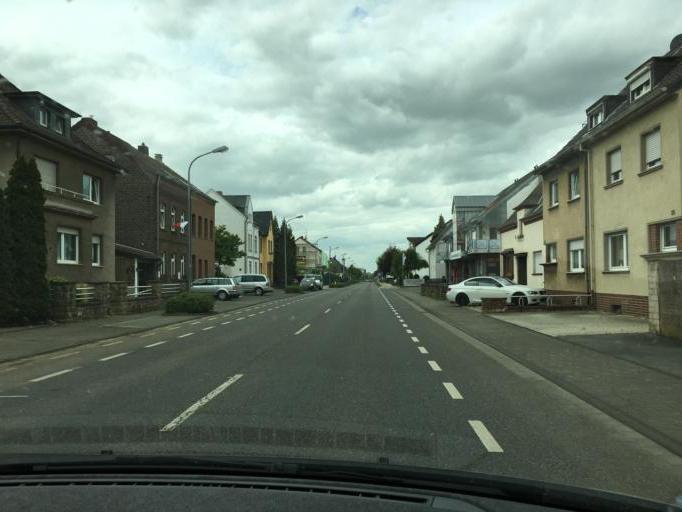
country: DE
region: North Rhine-Westphalia
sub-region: Regierungsbezirk Koln
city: Euskirchen
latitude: 50.6518
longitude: 6.8236
